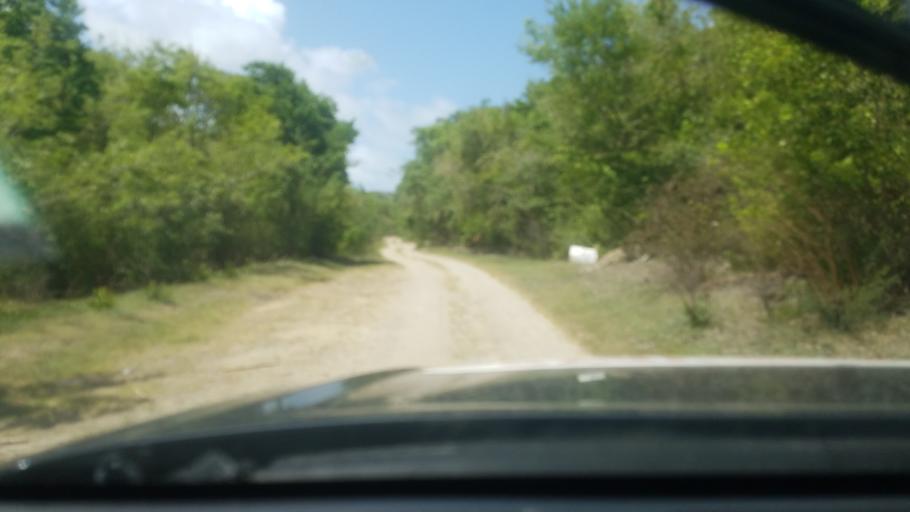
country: LC
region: Vieux-Fort
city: Vieux Fort
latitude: 13.7490
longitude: -60.9424
